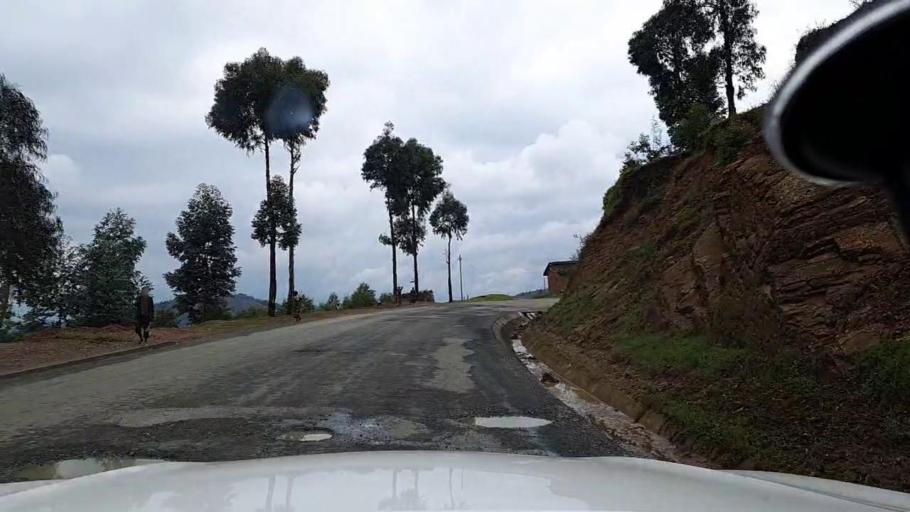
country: RW
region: Western Province
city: Kibuye
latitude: -2.0670
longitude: 29.5511
